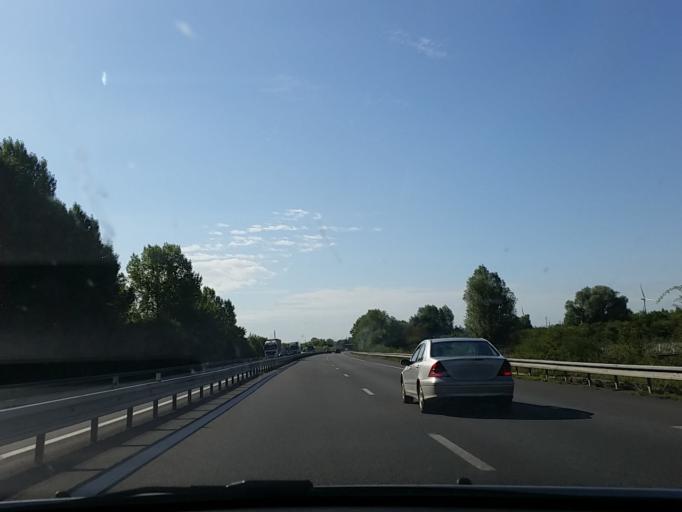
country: FR
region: Centre
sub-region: Departement du Cher
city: Foecy
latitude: 47.1705
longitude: 2.1804
